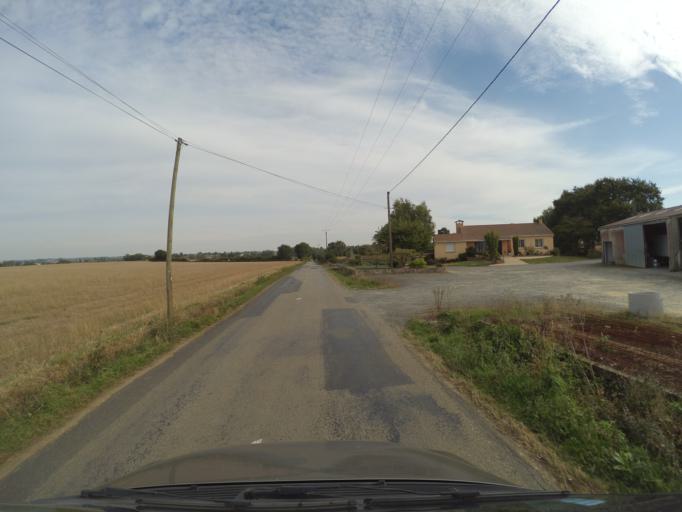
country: FR
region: Pays de la Loire
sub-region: Departement de Maine-et-Loire
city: La Chapelle-du-Genet
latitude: 47.1625
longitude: -0.9961
